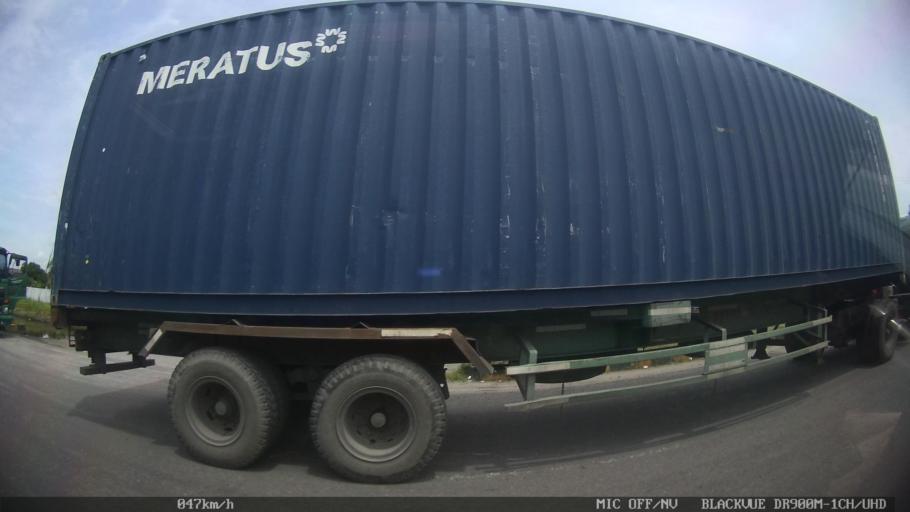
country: ID
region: North Sumatra
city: Belawan
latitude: 3.7782
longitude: 98.7030
